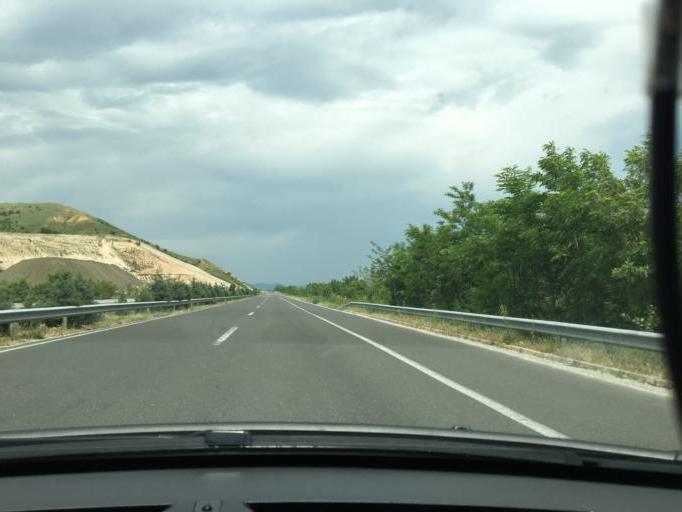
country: MK
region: Demir Kapija
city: Demir Kapija
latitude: 41.4338
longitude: 22.1827
